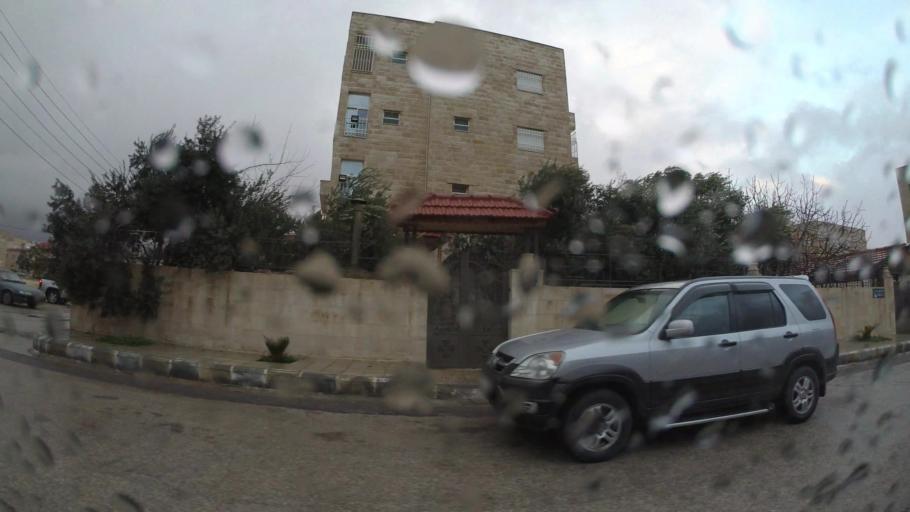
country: JO
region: Amman
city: Amman
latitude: 31.9977
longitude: 35.9207
